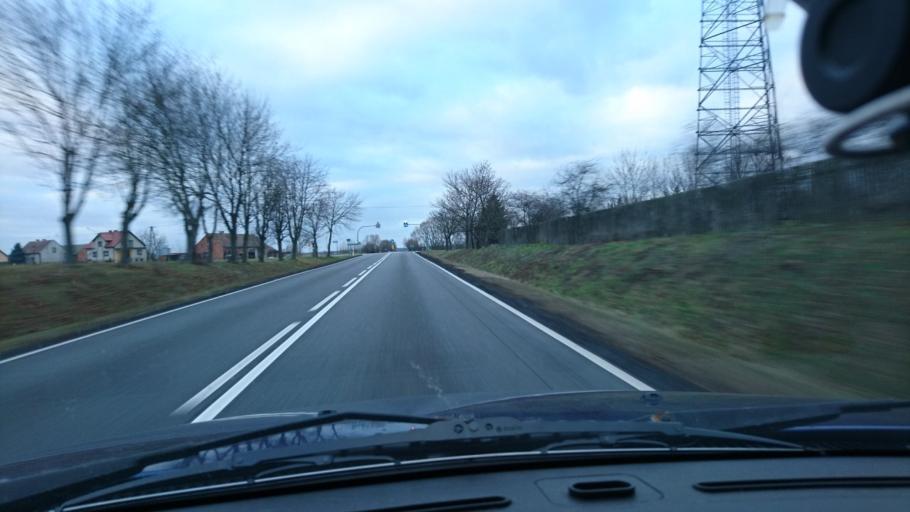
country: PL
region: Greater Poland Voivodeship
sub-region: Powiat kepinski
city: Opatow
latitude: 51.2128
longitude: 18.1432
